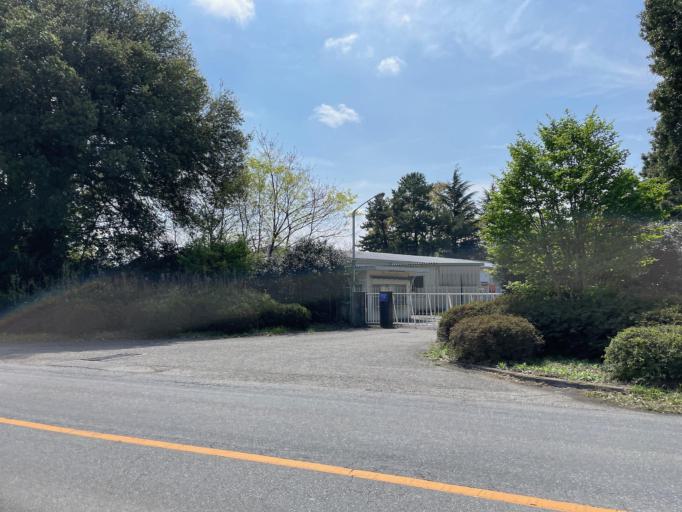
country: JP
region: Gunma
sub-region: Sawa-gun
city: Tamamura
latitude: 36.3034
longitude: 139.0778
